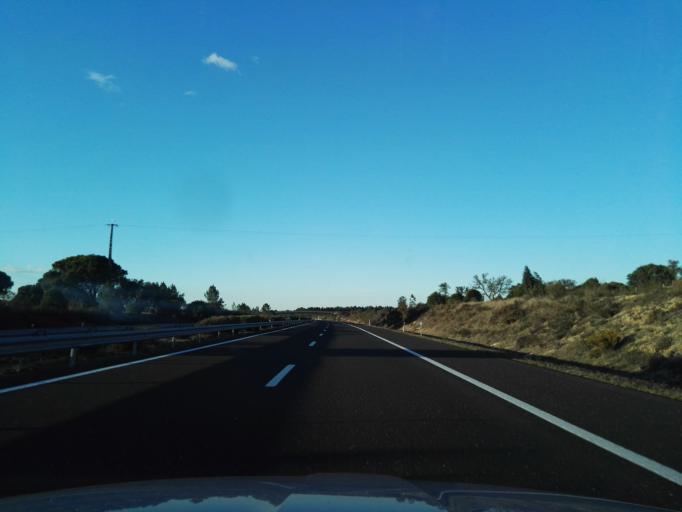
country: PT
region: Santarem
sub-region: Benavente
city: Poceirao
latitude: 38.7828
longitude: -8.6855
